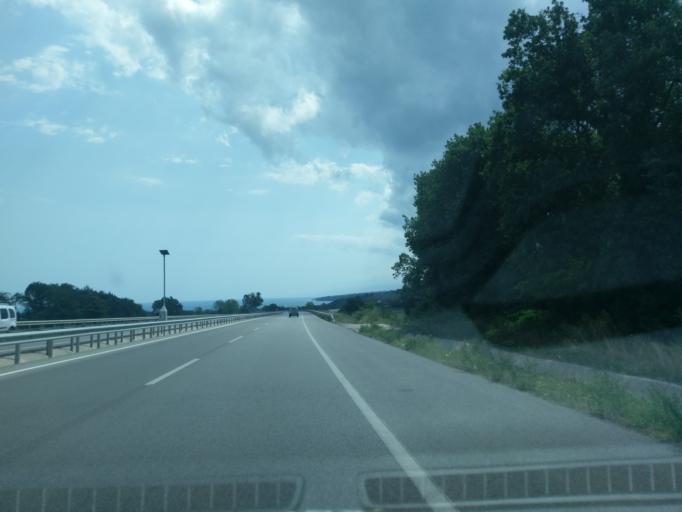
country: TR
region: Sinop
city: Kabali
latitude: 41.8451
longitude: 35.1376
